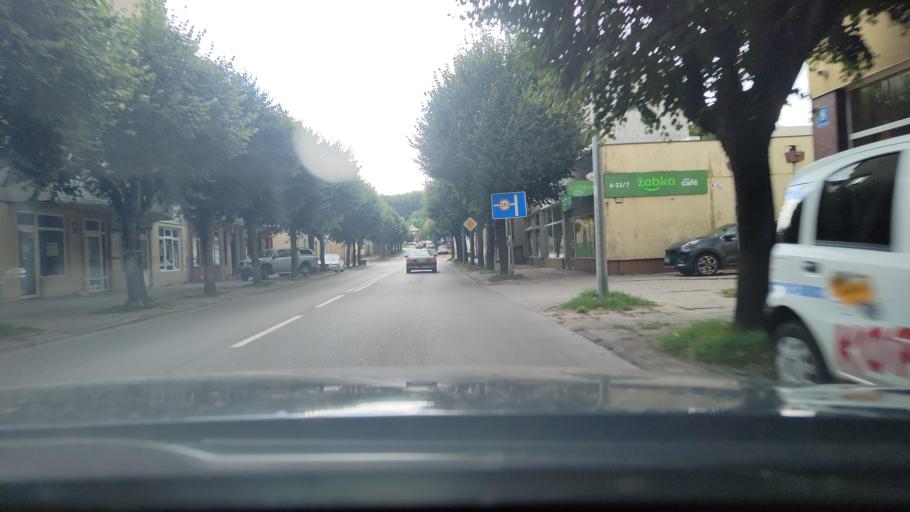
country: PL
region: Pomeranian Voivodeship
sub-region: Powiat wejherowski
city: Wejherowo
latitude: 54.5999
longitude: 18.2328
